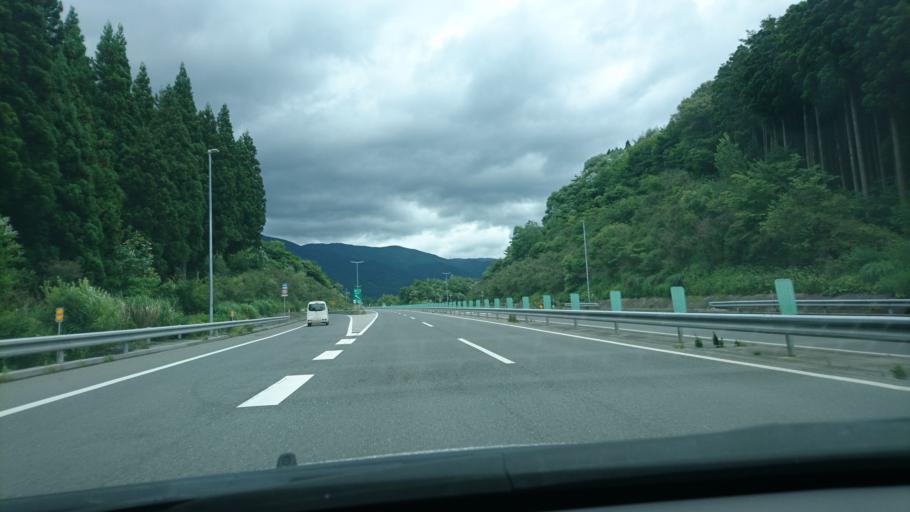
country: JP
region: Iwate
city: Ofunato
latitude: 39.1045
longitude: 141.7065
